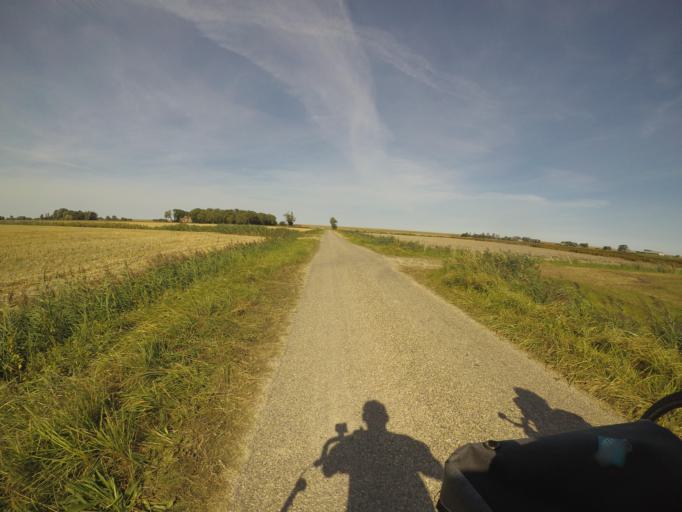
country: NL
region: Friesland
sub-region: Gemeente Ferwerderadiel
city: Ferwert
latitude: 53.3409
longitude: 5.8119
